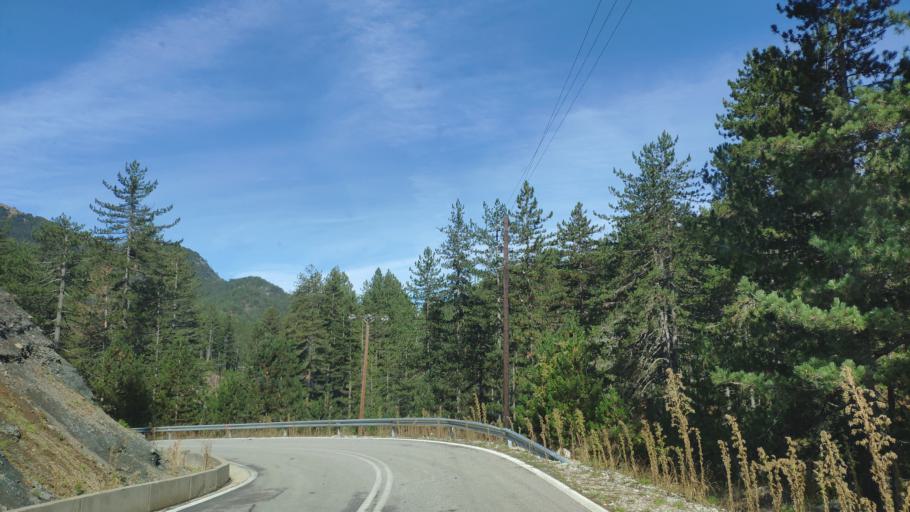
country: AL
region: Korce
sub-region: Rrethi i Devollit
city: Miras
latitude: 40.4027
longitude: 20.8816
